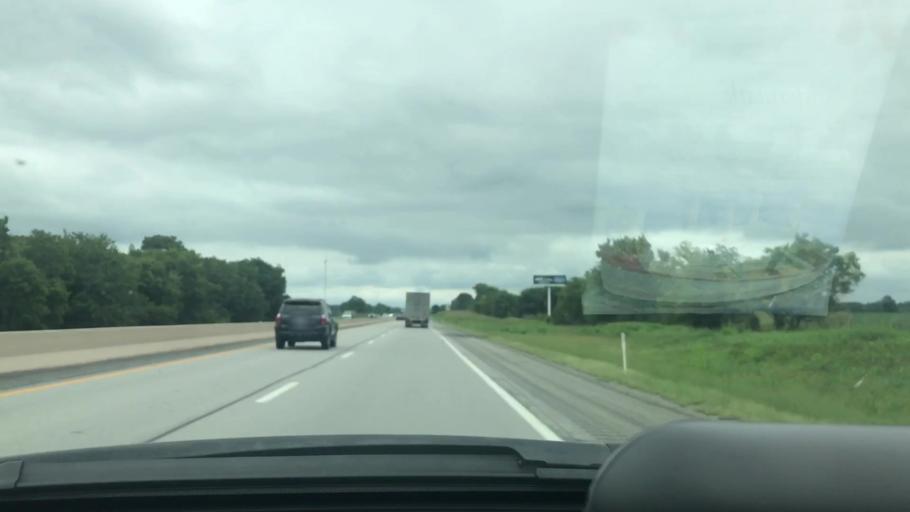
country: US
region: Oklahoma
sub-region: Ottawa County
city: Commerce
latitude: 36.9064
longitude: -94.7972
